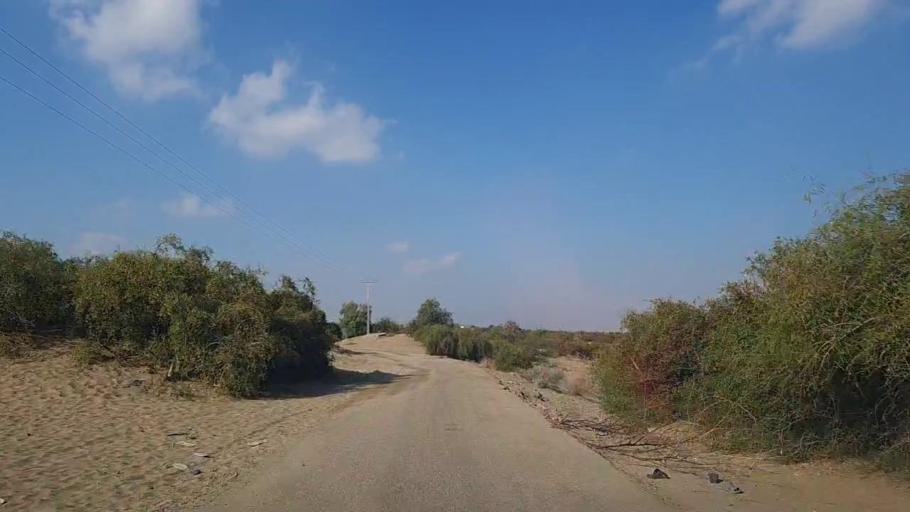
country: PK
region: Sindh
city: Tando Mittha Khan
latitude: 26.0107
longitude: 69.2486
